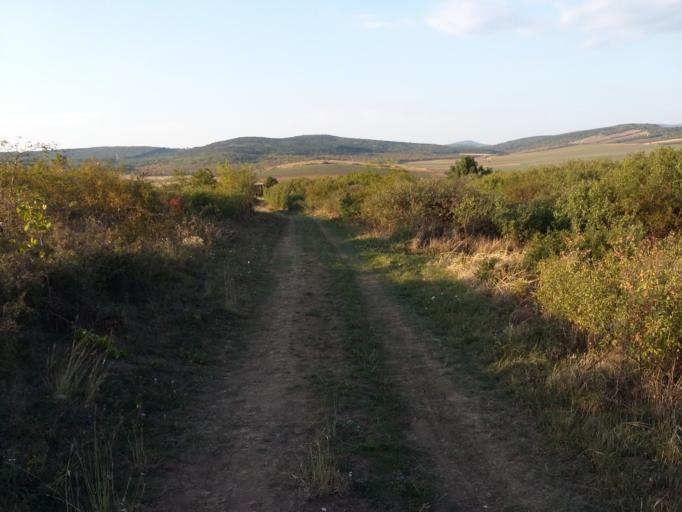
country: HU
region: Borsod-Abauj-Zemplen
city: Bekecs
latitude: 48.1589
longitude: 21.1731
